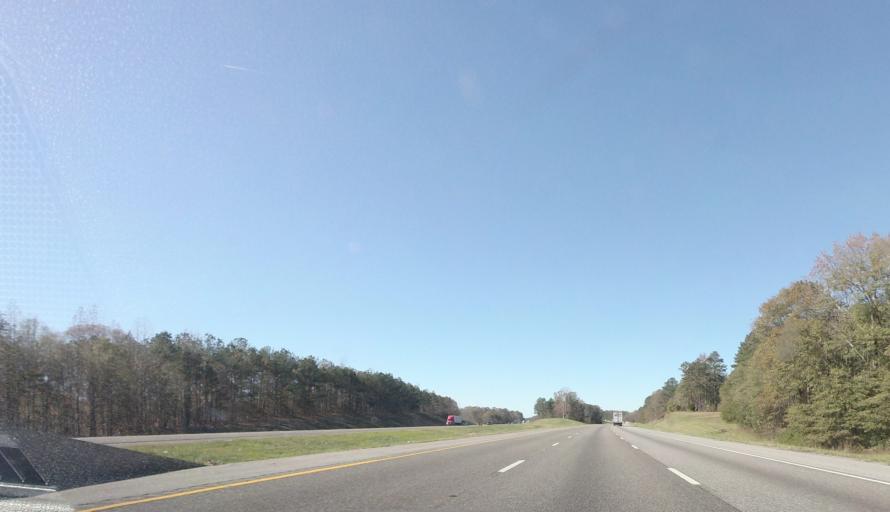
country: US
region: Alabama
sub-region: Calhoun County
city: Bynum
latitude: 33.5813
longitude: -85.9528
